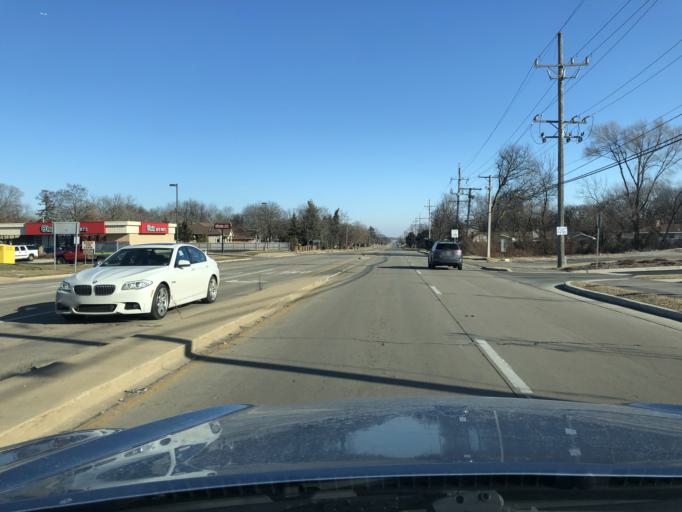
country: US
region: Illinois
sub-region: DuPage County
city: Roselle
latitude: 41.9978
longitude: -88.0799
